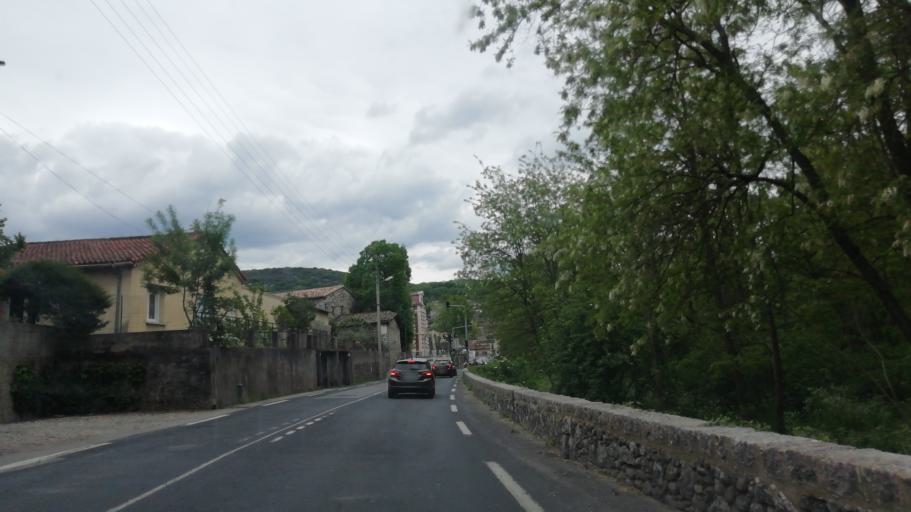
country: FR
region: Languedoc-Roussillon
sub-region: Departement de l'Herault
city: Laroque
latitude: 43.9249
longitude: 3.7199
